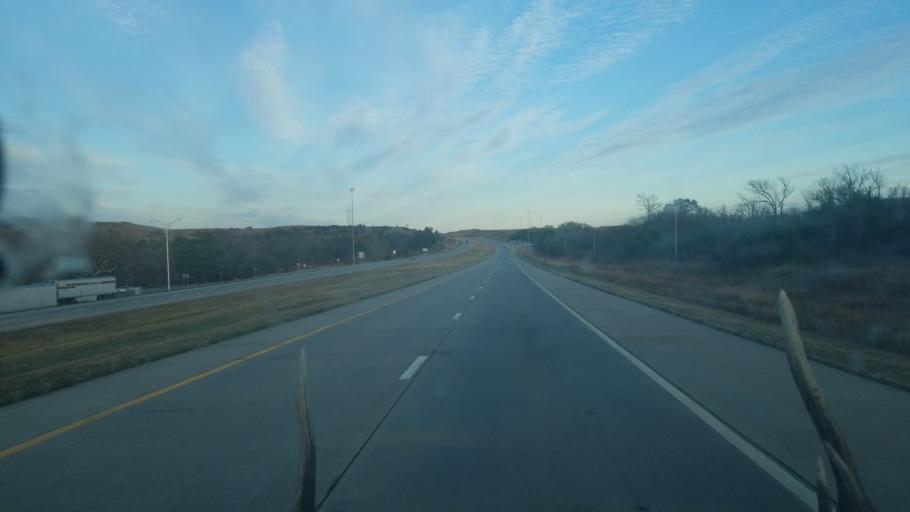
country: US
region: Kansas
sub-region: Riley County
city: Ogden
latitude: 39.0663
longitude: -96.6236
